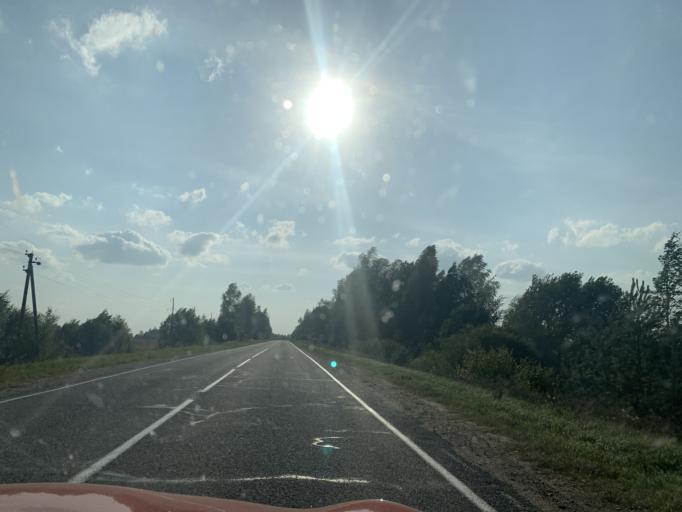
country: BY
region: Minsk
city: Ivyanyets
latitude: 53.8670
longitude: 26.7293
